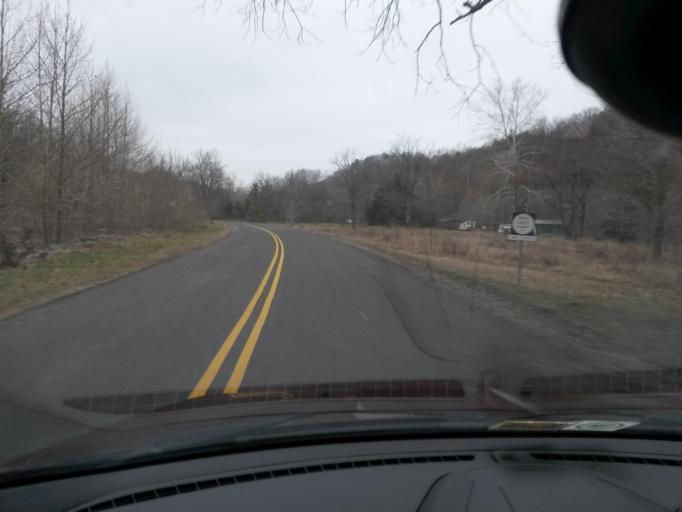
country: US
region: Virginia
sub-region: City of Buena Vista
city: Buena Vista
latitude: 37.8468
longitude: -79.2767
